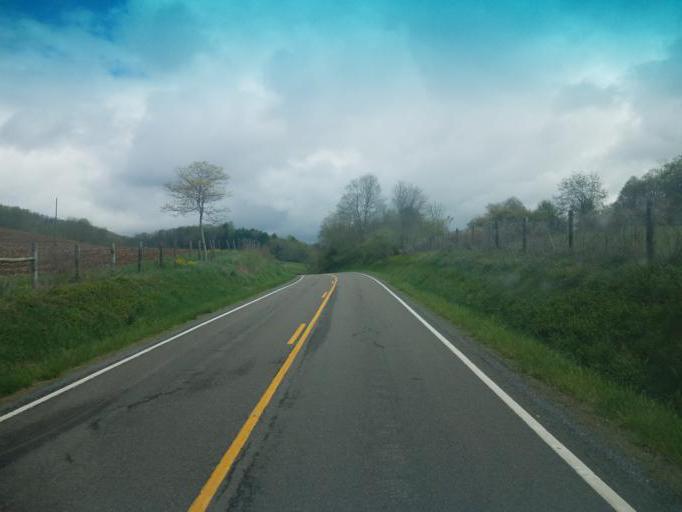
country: US
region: Virginia
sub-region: Wythe County
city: Rural Retreat
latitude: 37.0136
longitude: -81.3555
